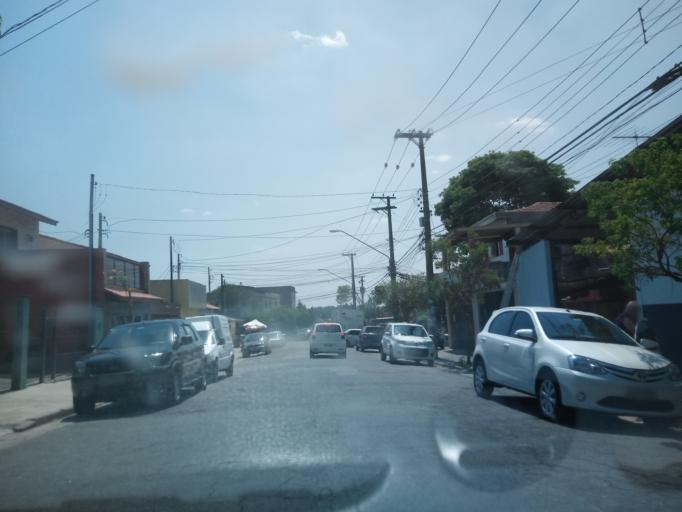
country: BR
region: Sao Paulo
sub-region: Sao Bernardo Do Campo
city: Sao Bernardo do Campo
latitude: -23.7203
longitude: -46.5721
